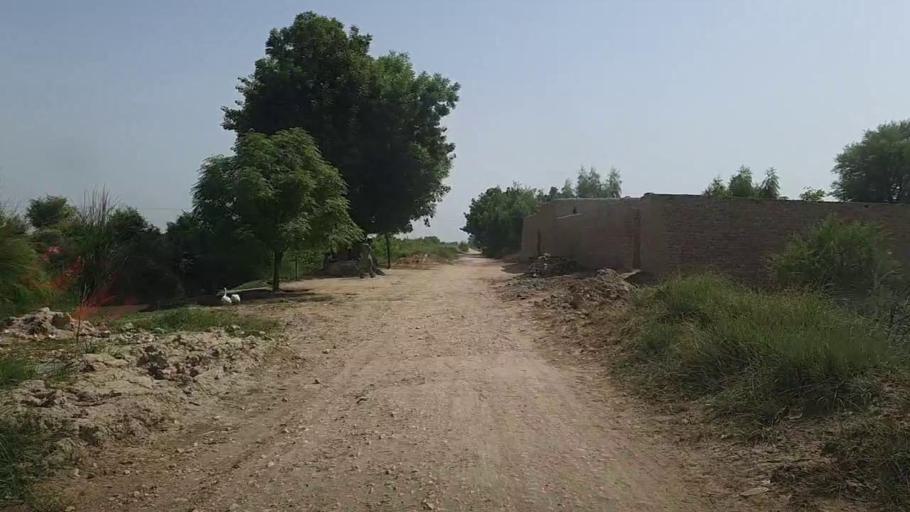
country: PK
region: Sindh
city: Pad Idan
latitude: 26.7941
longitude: 68.3291
